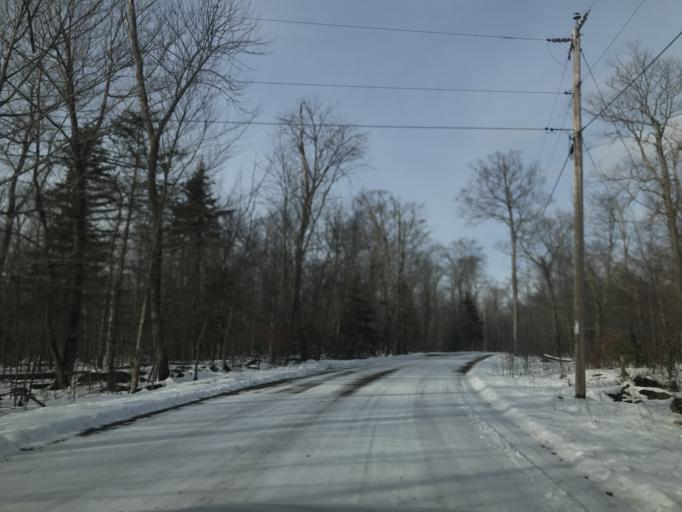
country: US
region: Wisconsin
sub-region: Door County
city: Sturgeon Bay
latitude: 45.1435
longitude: -87.0534
